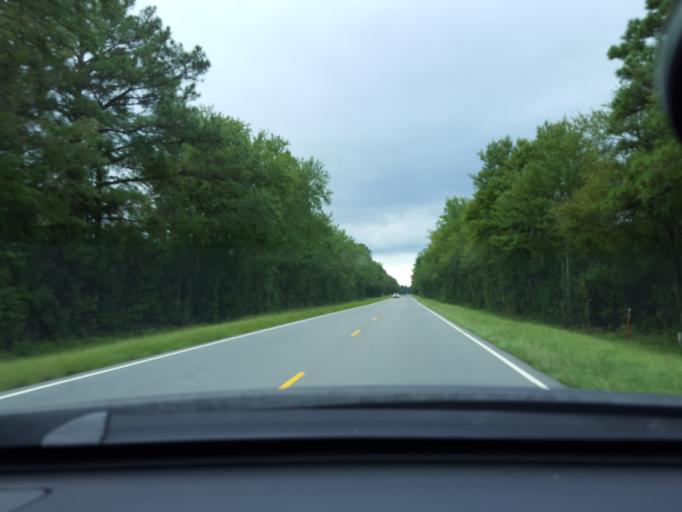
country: US
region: North Carolina
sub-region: Bladen County
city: Elizabethtown
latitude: 34.7286
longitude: -78.4382
